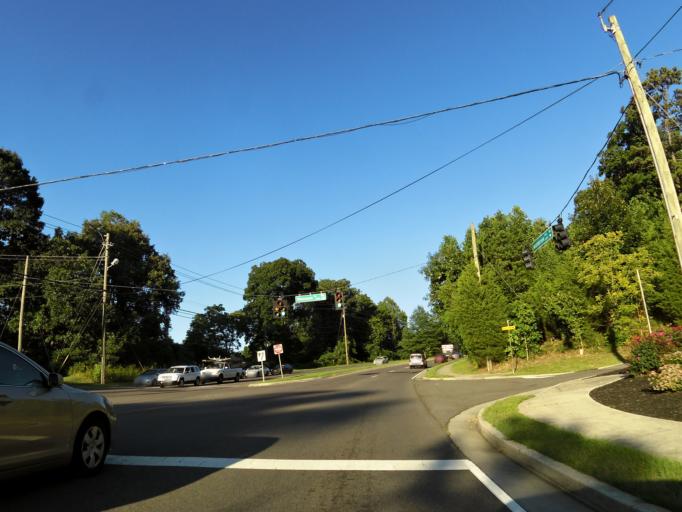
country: US
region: Tennessee
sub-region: Knox County
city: Farragut
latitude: 35.9441
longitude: -84.0567
